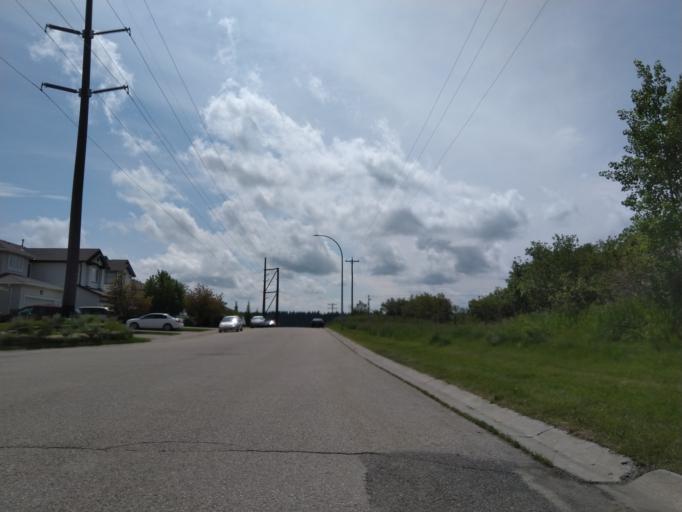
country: CA
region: Alberta
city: Cochrane
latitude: 51.1848
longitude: -114.5133
